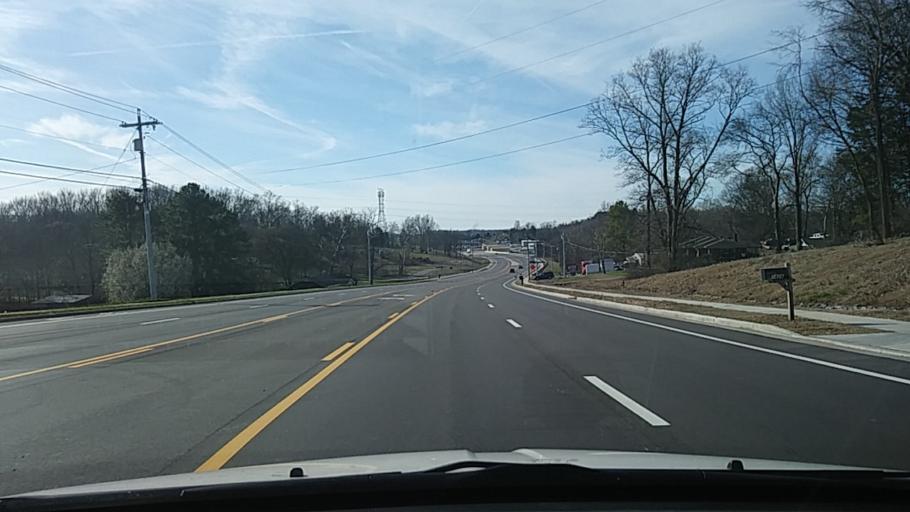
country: US
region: Tennessee
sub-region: Sumner County
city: Gallatin
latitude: 36.3515
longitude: -86.4385
